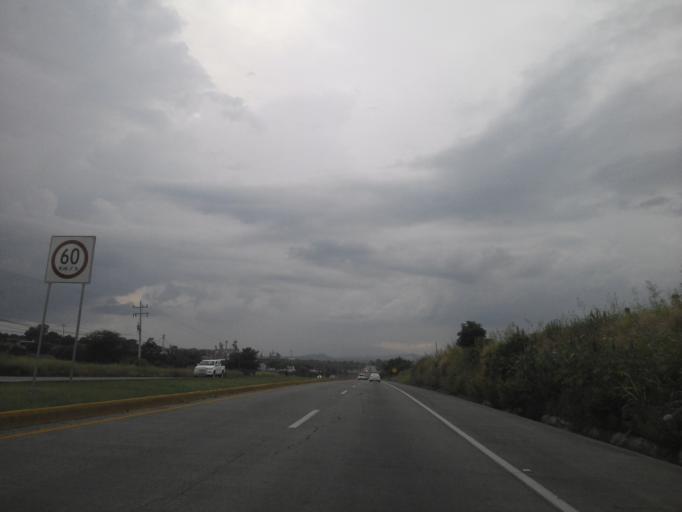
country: MX
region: Jalisco
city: Zapotlanejo
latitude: 20.6038
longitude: -103.0945
